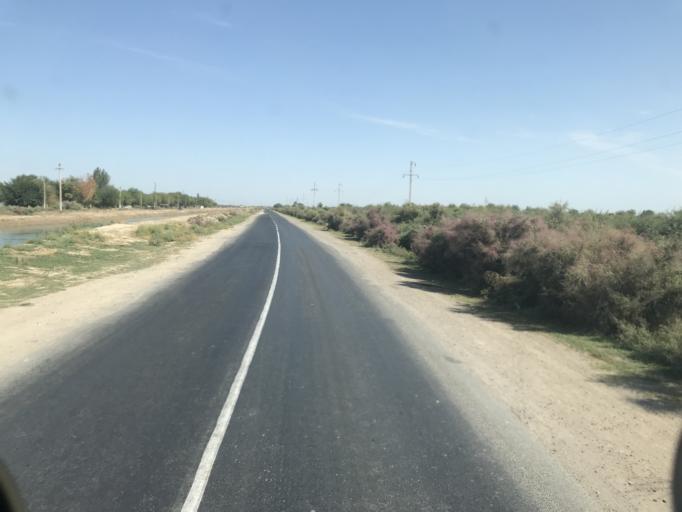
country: KZ
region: Ongtustik Qazaqstan
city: Myrzakent
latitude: 40.7169
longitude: 68.5344
